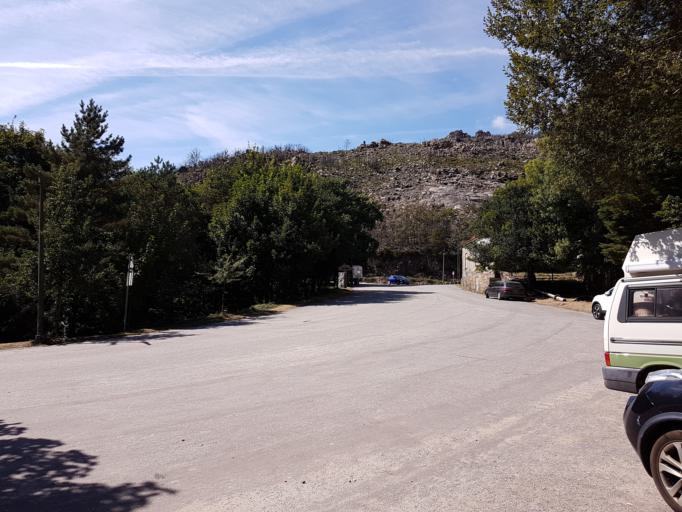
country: ES
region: Galicia
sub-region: Provincia de Ourense
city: Lobios
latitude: 41.8083
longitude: -8.1304
